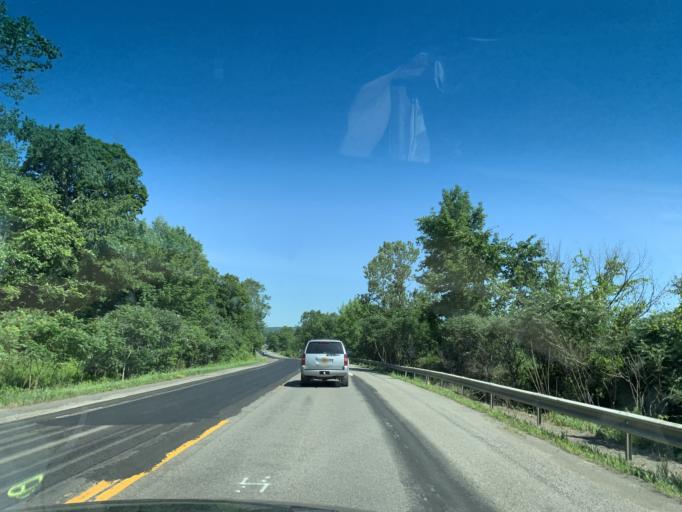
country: US
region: New York
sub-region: Delaware County
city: Sidney
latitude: 42.3602
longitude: -75.4016
